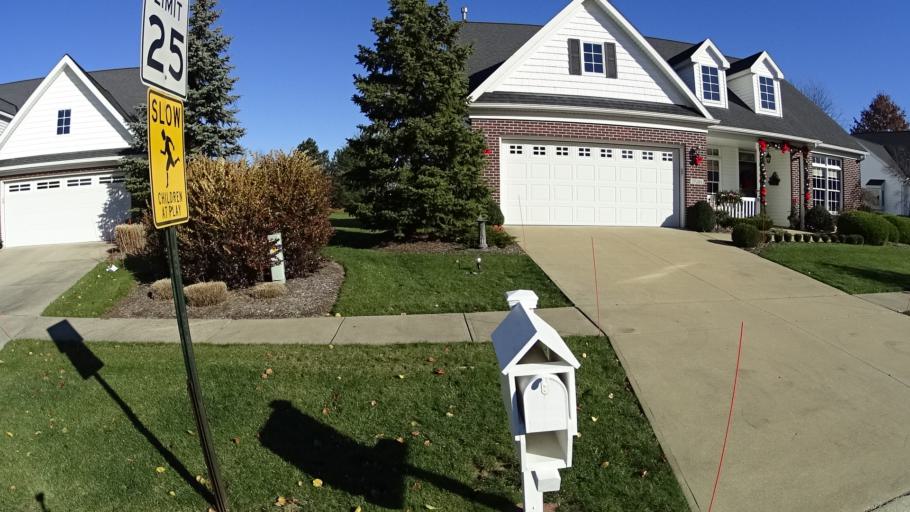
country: US
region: Ohio
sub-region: Lorain County
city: Sheffield
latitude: 41.4200
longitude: -82.0632
